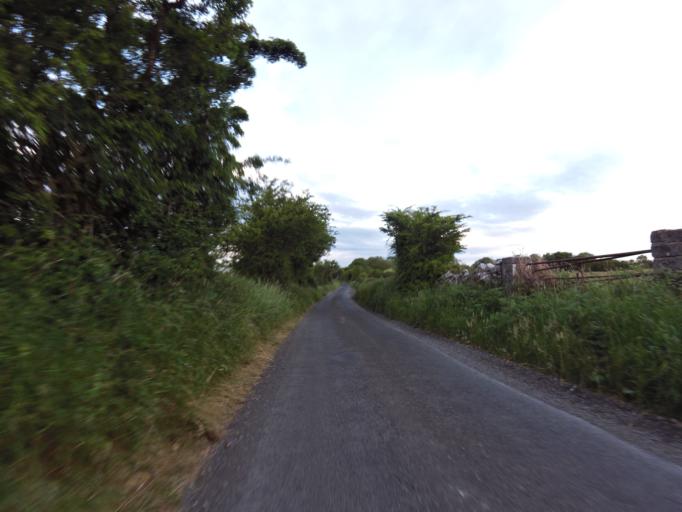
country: IE
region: Connaught
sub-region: County Galway
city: Athenry
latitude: 53.2846
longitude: -8.7208
